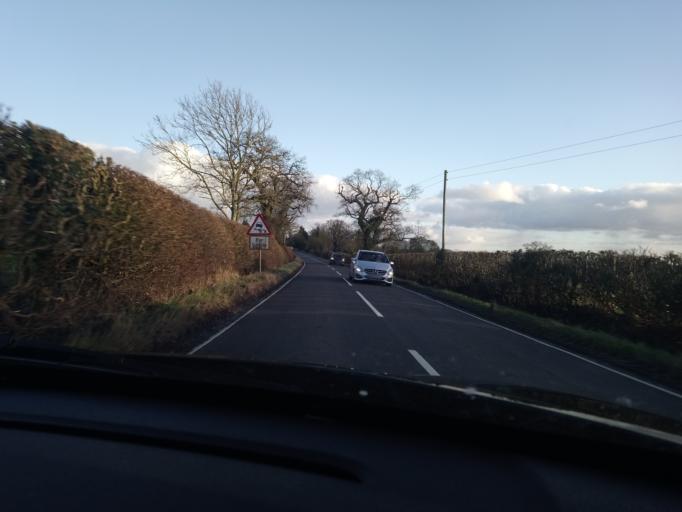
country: GB
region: England
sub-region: Shropshire
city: Wem
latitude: 52.8685
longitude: -2.7709
